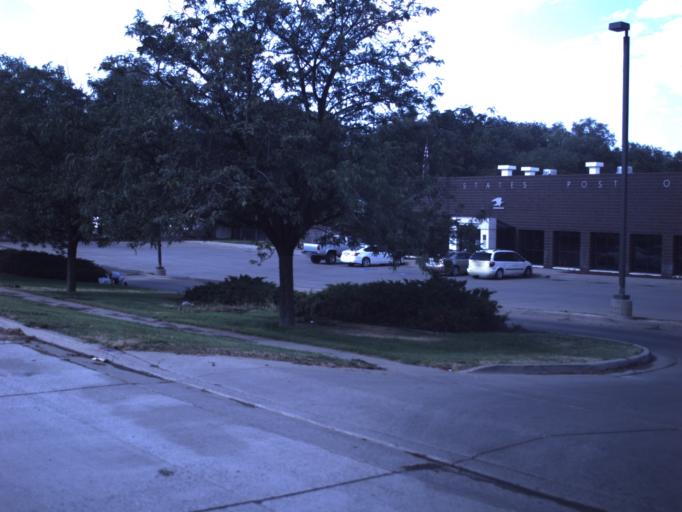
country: US
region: Utah
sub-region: Weber County
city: Harrisville
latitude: 41.2640
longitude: -111.9697
